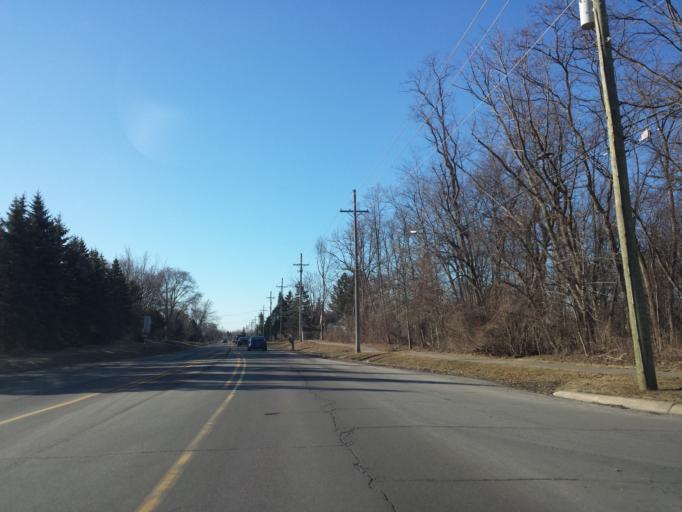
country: US
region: Michigan
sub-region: Oakland County
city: Troy
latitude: 42.6290
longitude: -83.1519
